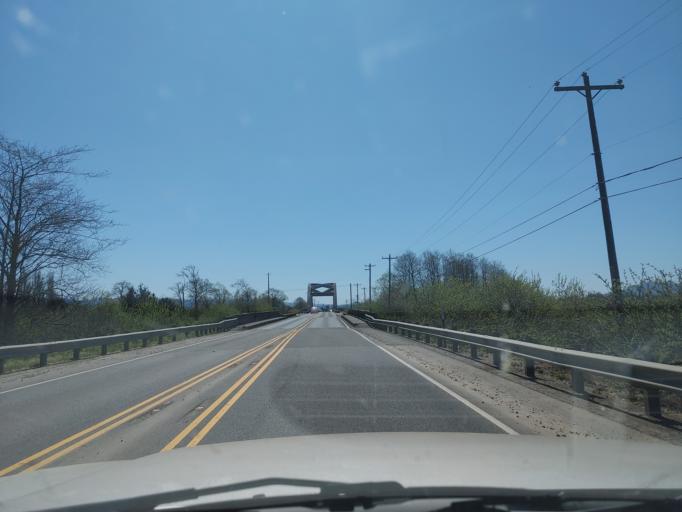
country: US
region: Oregon
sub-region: Tillamook County
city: Tillamook
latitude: 45.4782
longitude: -123.8449
